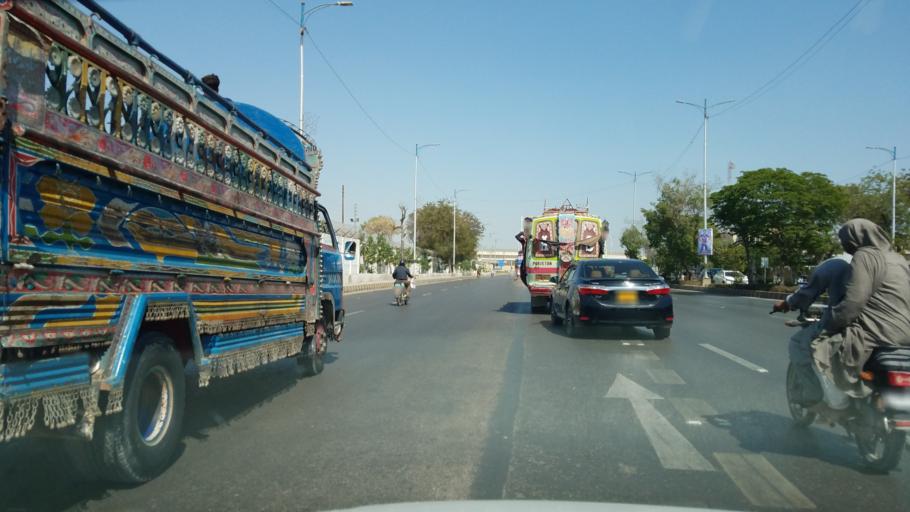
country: PK
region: Sindh
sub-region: Karachi District
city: Karachi
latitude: 24.8859
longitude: 67.1228
